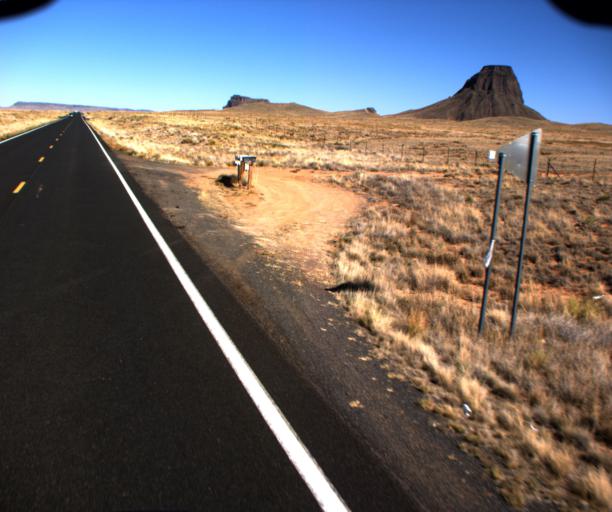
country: US
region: Arizona
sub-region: Navajo County
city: Dilkon
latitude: 35.2883
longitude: -110.4271
